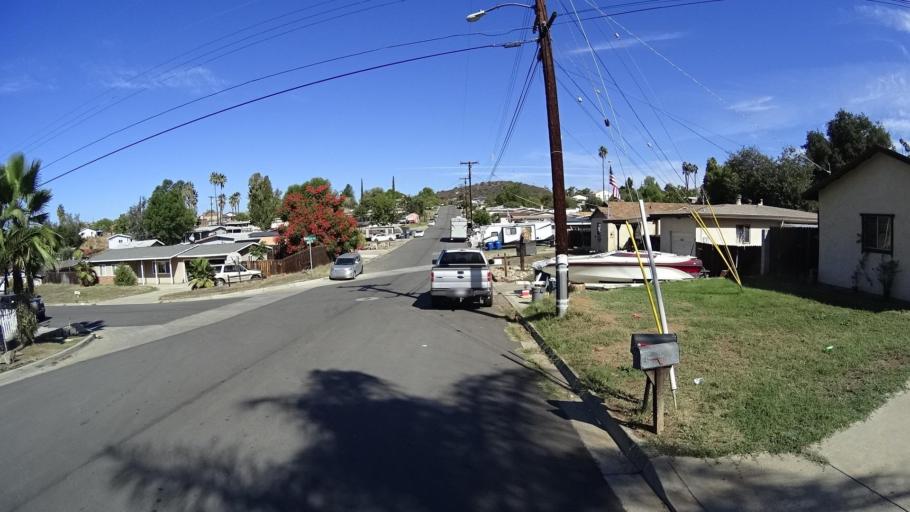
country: US
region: California
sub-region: San Diego County
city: Lakeside
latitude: 32.8391
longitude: -116.9006
